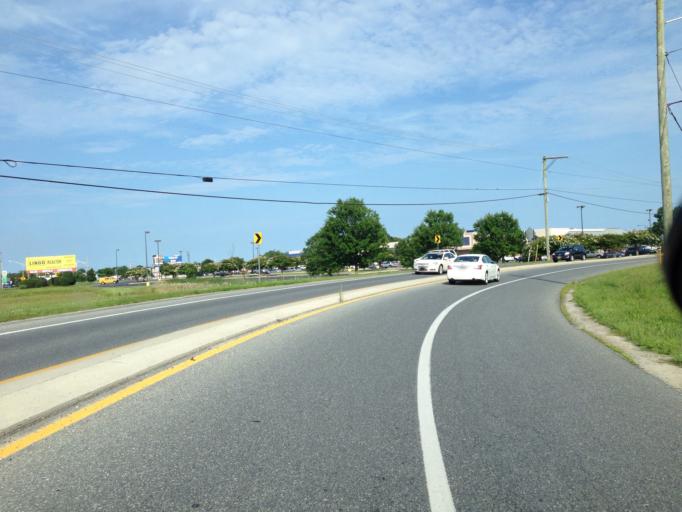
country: US
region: Delaware
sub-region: Sussex County
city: Lewes
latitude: 38.7477
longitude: -75.1744
